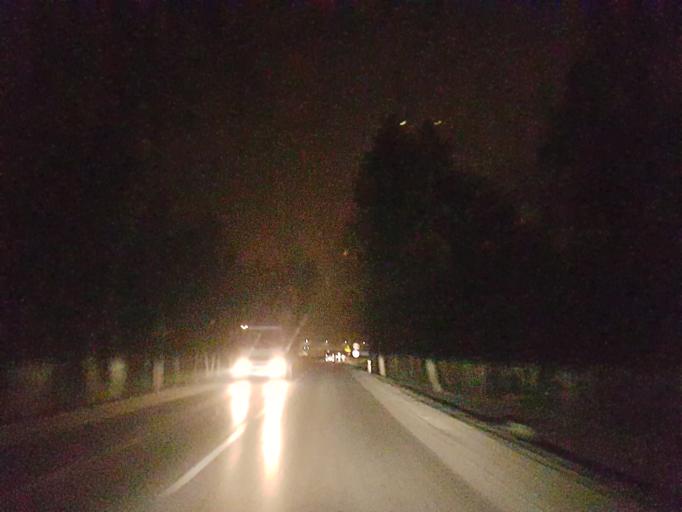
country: PL
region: Masovian Voivodeship
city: Zielonka
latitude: 52.3288
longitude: 21.1441
